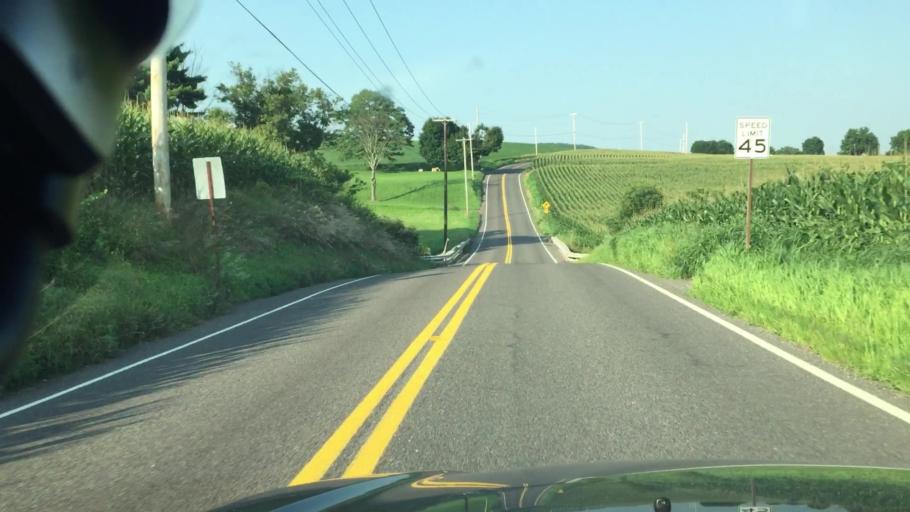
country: US
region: Pennsylvania
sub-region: Columbia County
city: Almedia
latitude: 40.9854
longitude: -76.3618
